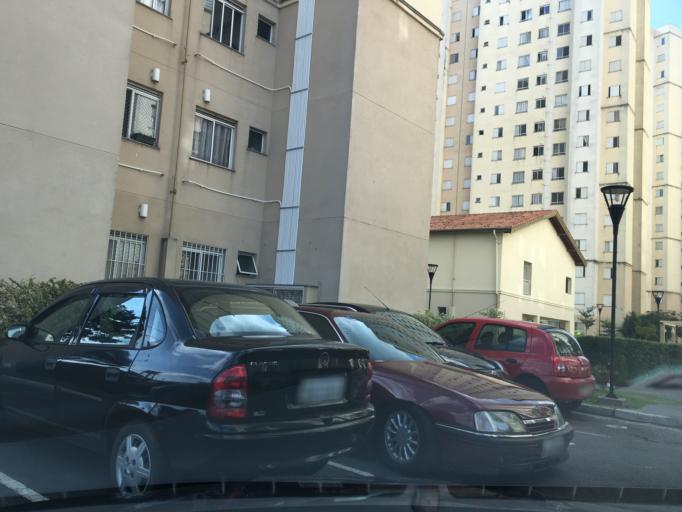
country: BR
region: Sao Paulo
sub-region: Guarulhos
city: Guarulhos
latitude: -23.4935
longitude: -46.5428
